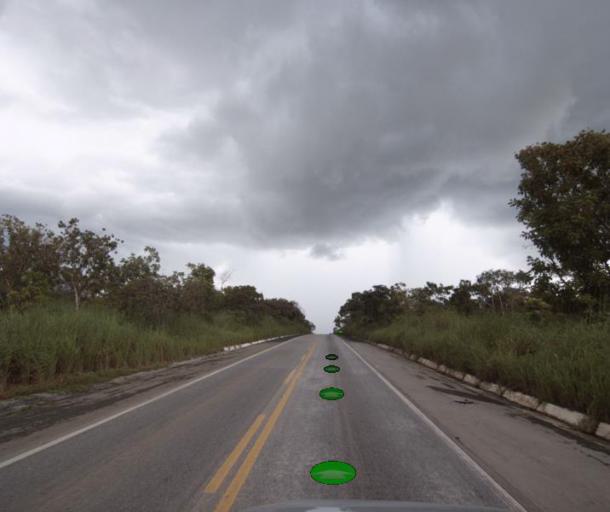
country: BR
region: Goias
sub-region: Uruacu
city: Uruacu
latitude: -14.2232
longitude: -49.1326
